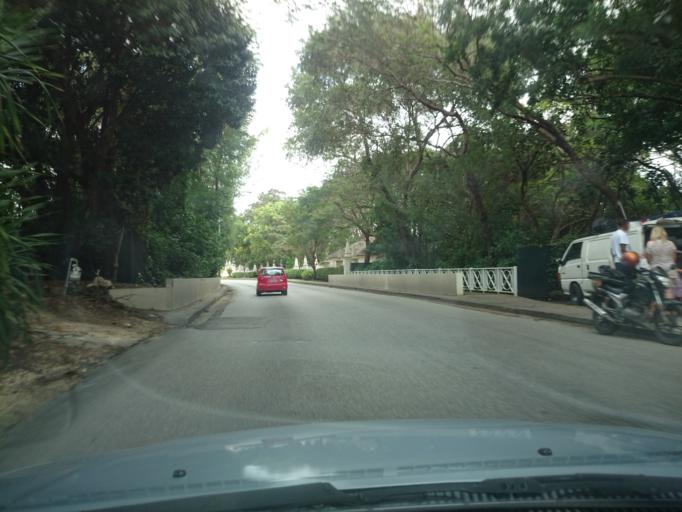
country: BB
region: Saint James
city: Holetown
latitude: 13.1719
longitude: -59.6361
